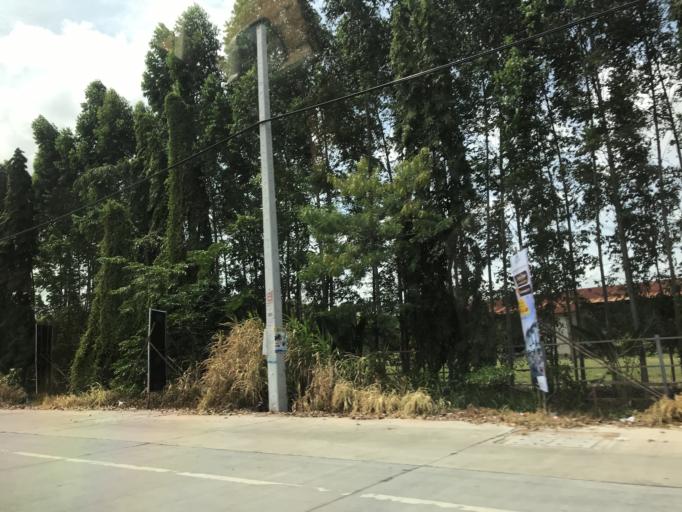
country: TH
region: Chon Buri
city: Si Racha
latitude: 13.1496
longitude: 100.9680
